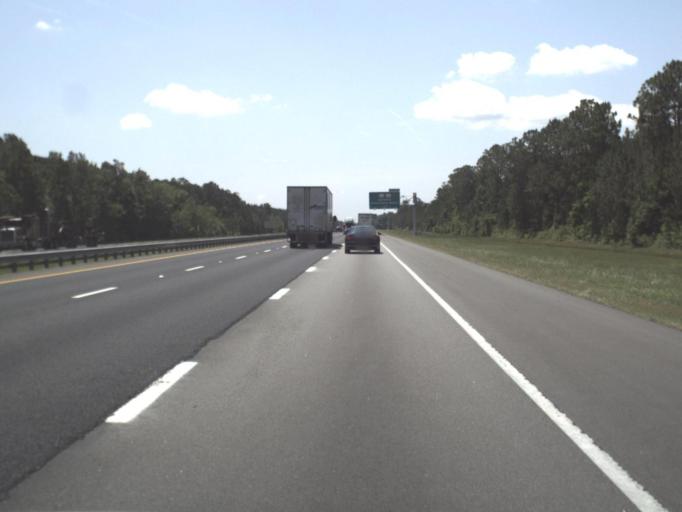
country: US
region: Florida
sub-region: Nassau County
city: Yulee
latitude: 30.6383
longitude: -81.6568
